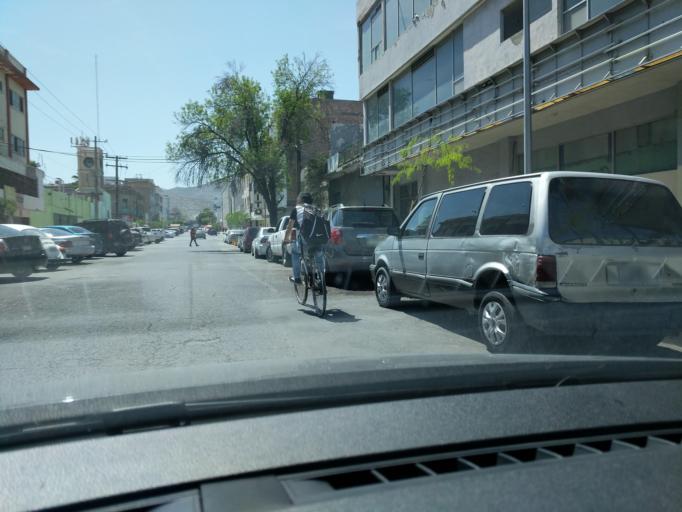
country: MX
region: Durango
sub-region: Lerdo
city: El Huarache (El Guarache)
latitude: 25.5384
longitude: -103.4649
